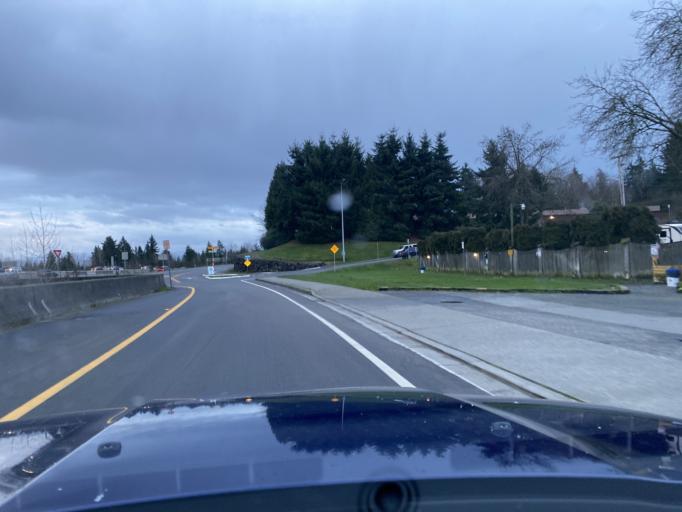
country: US
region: Washington
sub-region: King County
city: Eastgate
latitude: 47.5776
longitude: -122.1330
